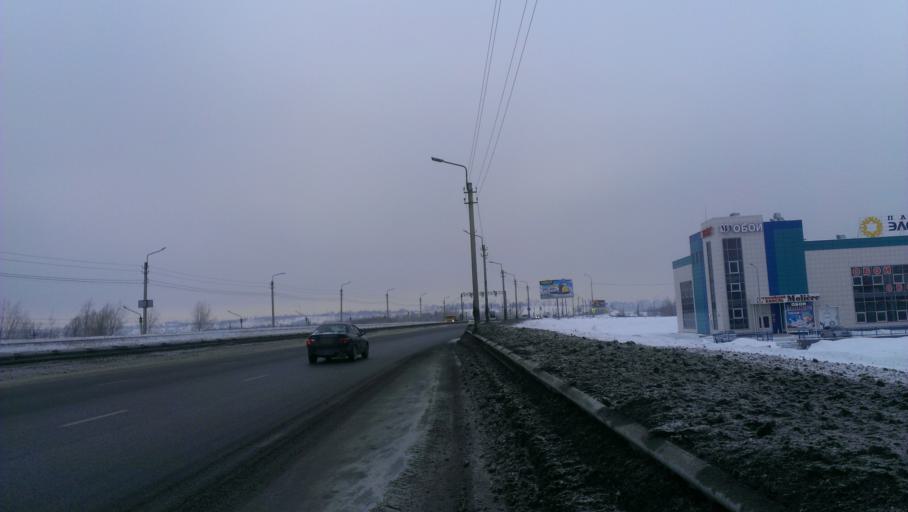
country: RU
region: Altai Krai
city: Zaton
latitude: 53.3160
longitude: 83.8262
